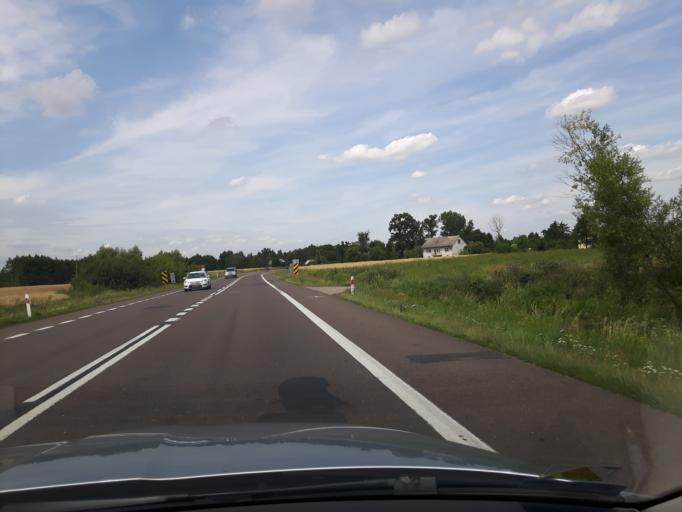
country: PL
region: Masovian Voivodeship
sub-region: Powiat ciechanowski
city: Glinojeck
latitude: 52.7984
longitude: 20.2702
